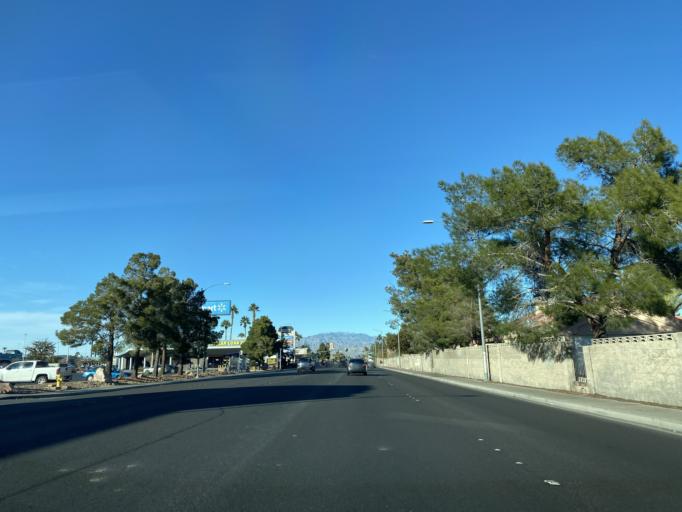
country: US
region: Nevada
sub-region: Clark County
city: Spring Valley
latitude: 36.2140
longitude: -115.2423
